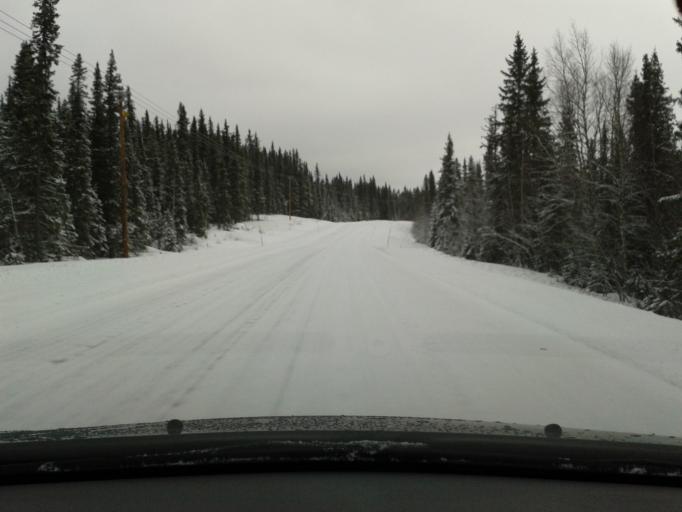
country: SE
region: Vaesterbotten
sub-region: Vilhelmina Kommun
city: Sjoberg
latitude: 65.2369
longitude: 15.8290
